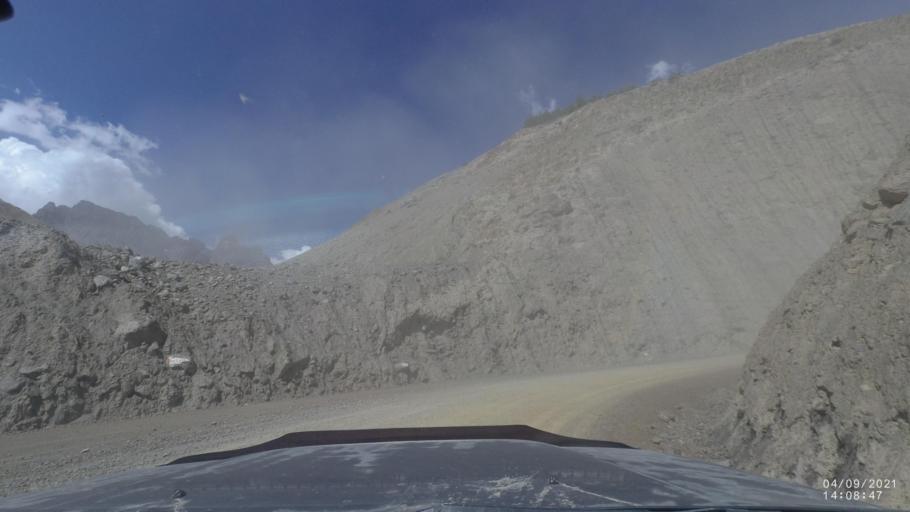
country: BO
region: Cochabamba
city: Sipe Sipe
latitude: -17.2249
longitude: -66.4615
